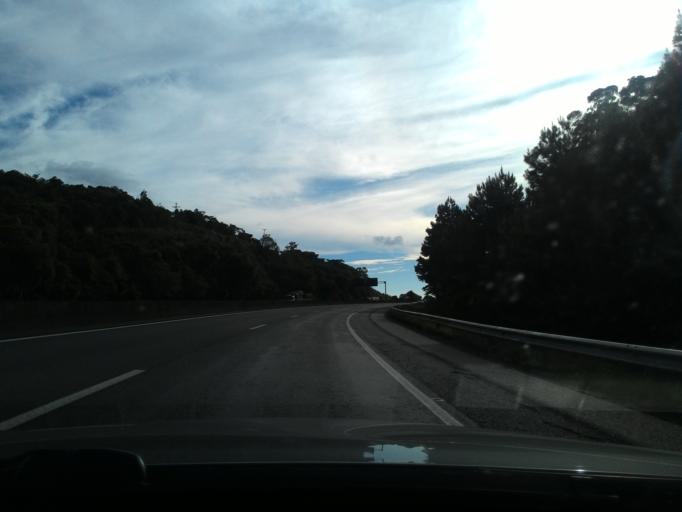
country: BR
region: Parana
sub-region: Campina Grande Do Sul
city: Campina Grande do Sul
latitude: -25.1750
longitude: -48.8694
